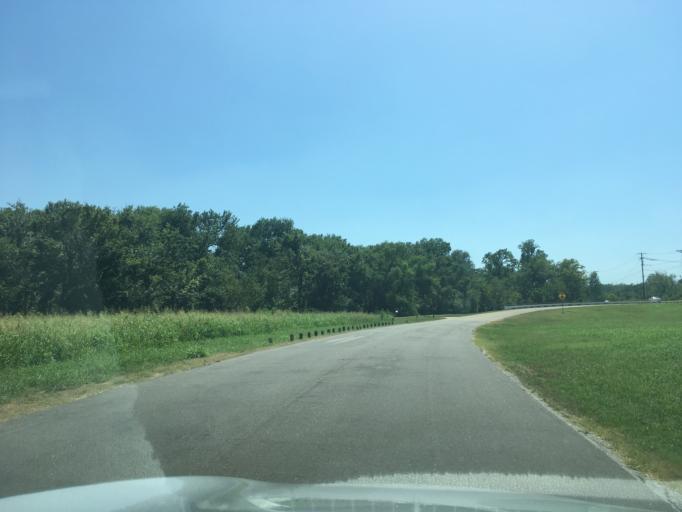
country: US
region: Texas
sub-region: Dallas County
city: Highland Park
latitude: 32.8588
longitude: -96.7221
